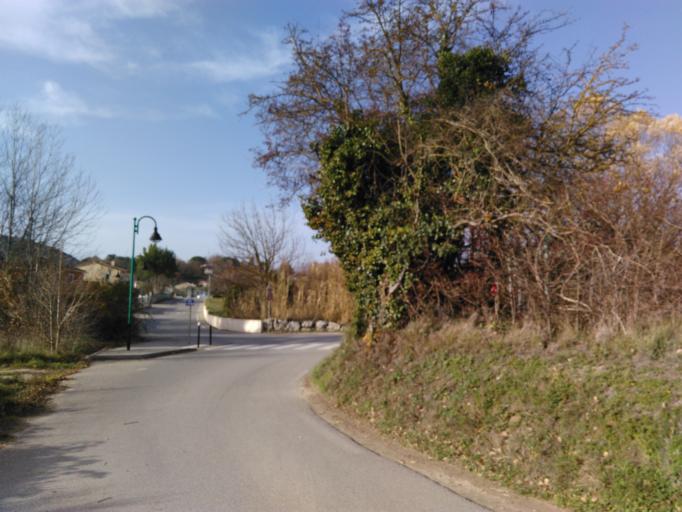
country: FR
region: Provence-Alpes-Cote d'Azur
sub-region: Departement du Vaucluse
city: Vaison-la-Romaine
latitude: 44.2400
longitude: 5.0894
